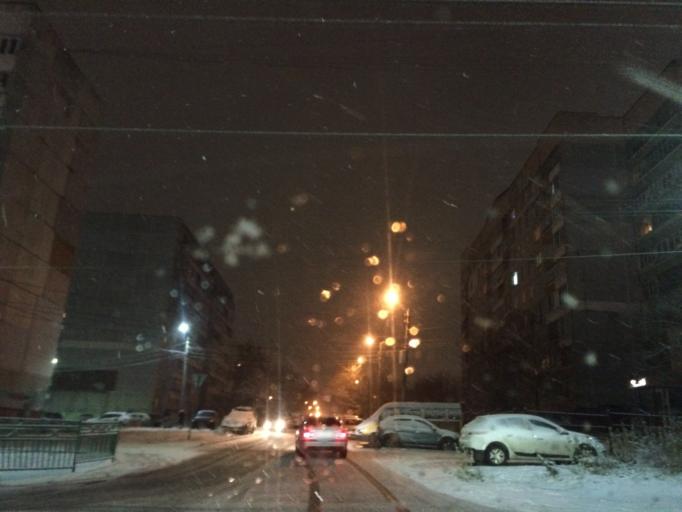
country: RU
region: Tula
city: Tula
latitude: 54.1981
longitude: 37.6384
